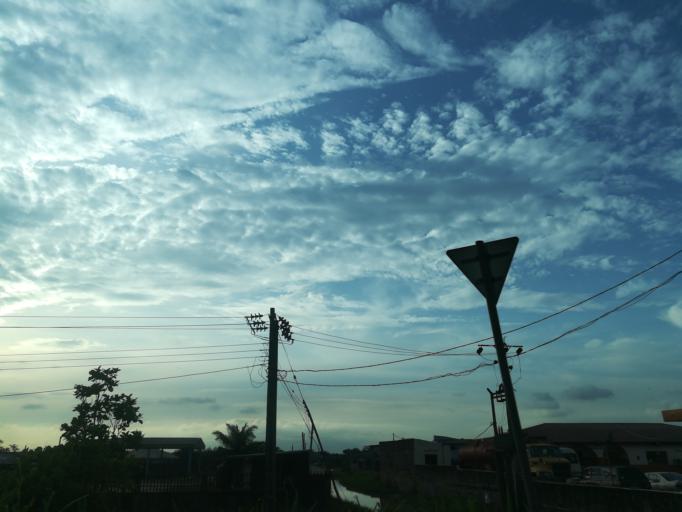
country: NG
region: Lagos
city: Ebute Ikorodu
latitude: 6.6145
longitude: 3.4429
